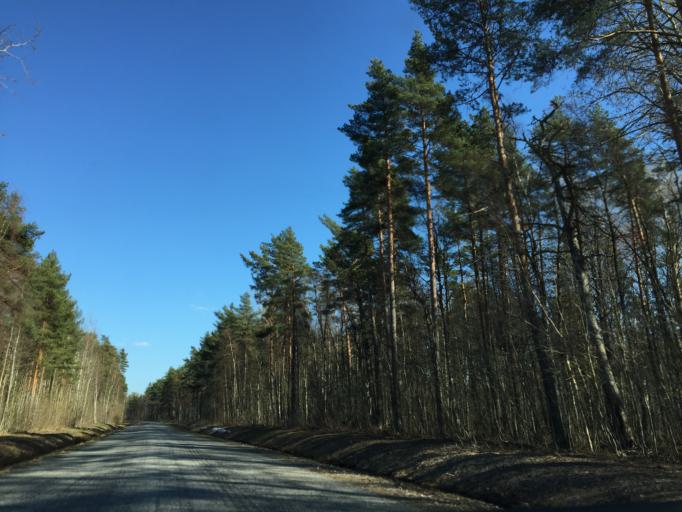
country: RU
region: Pskov
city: Gdov
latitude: 59.0065
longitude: 27.6694
